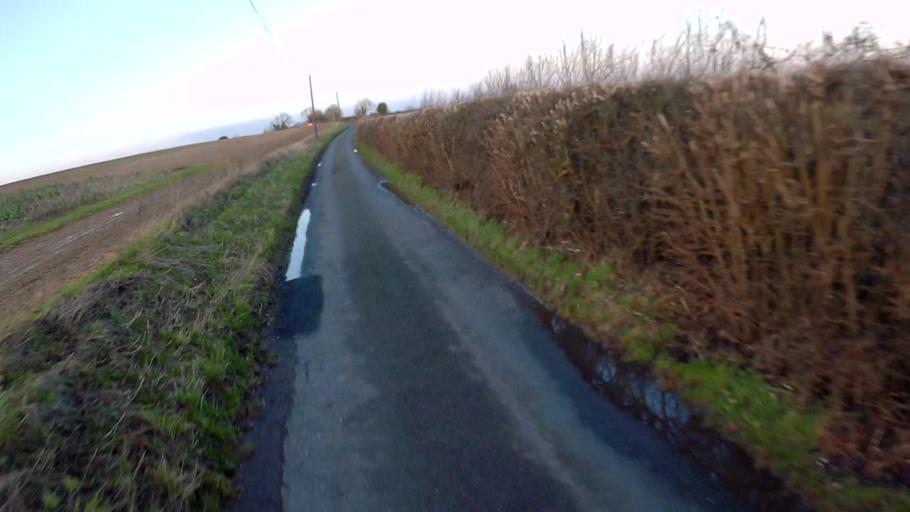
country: GB
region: England
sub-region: Hampshire
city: Overton
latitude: 51.2245
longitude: -1.2398
